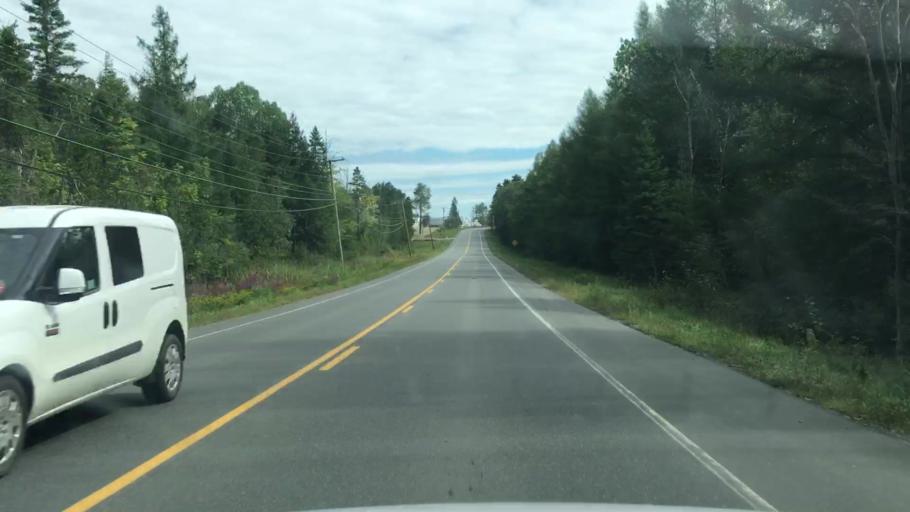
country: US
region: Maine
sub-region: Piscataquis County
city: Dover-Foxcroft
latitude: 45.1995
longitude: -69.2020
